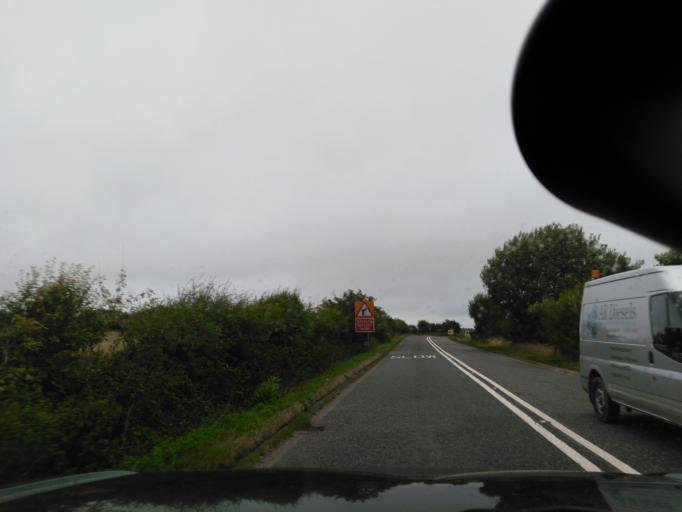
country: GB
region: England
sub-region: Wiltshire
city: Hindon
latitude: 51.0867
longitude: -2.1667
